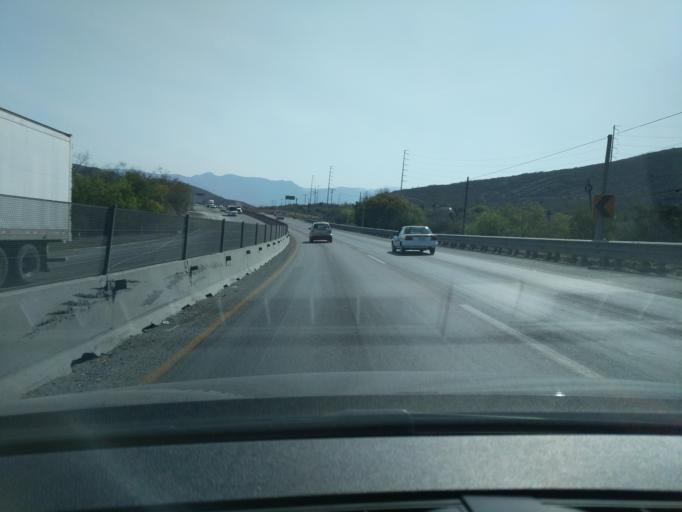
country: MX
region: Nuevo Leon
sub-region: Garcia
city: Los Parques
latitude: 25.7607
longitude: -100.4964
